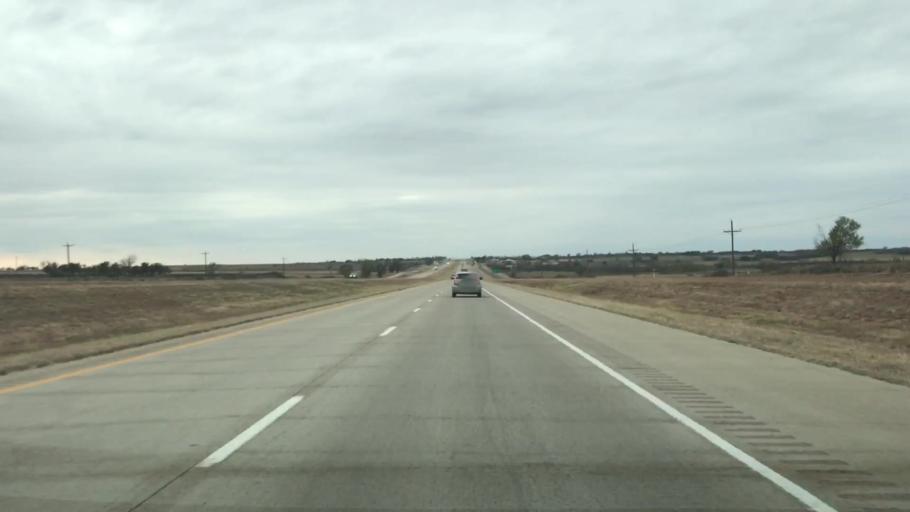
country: US
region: Texas
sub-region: Wheeler County
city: Shamrock
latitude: 35.2270
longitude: -100.1445
